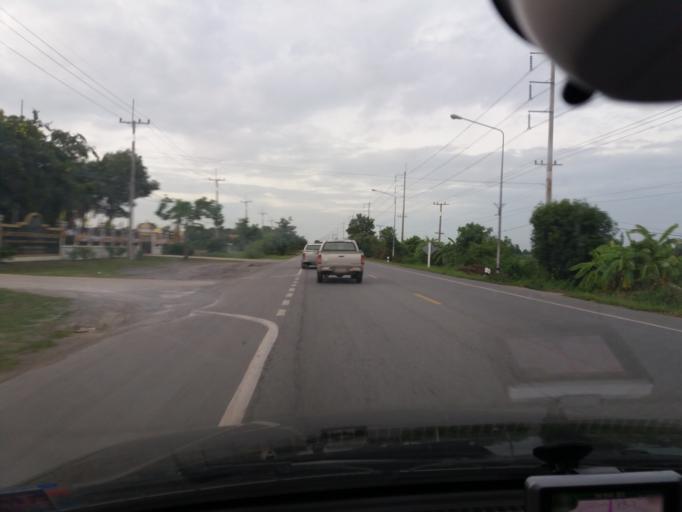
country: TH
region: Suphan Buri
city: U Thong
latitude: 14.5070
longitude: 99.9170
